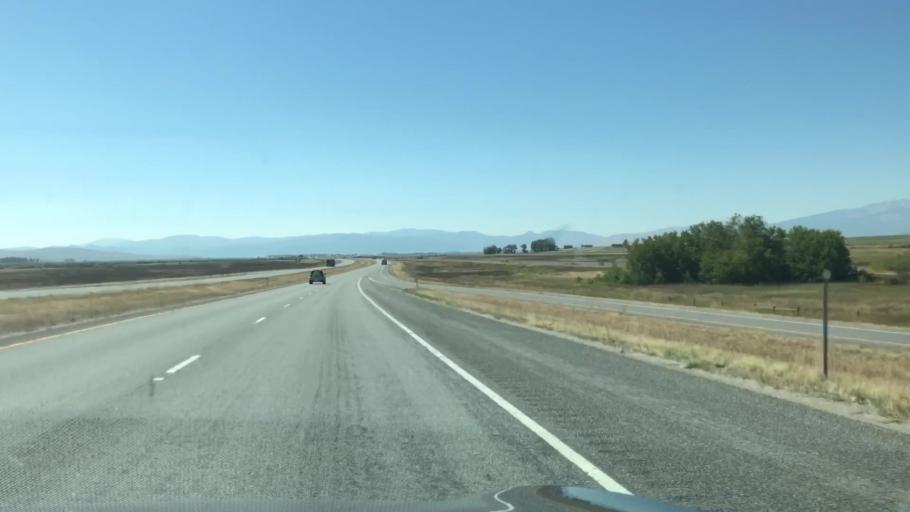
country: US
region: Montana
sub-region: Deer Lodge County
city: Warm Springs
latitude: 46.2360
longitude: -112.7649
